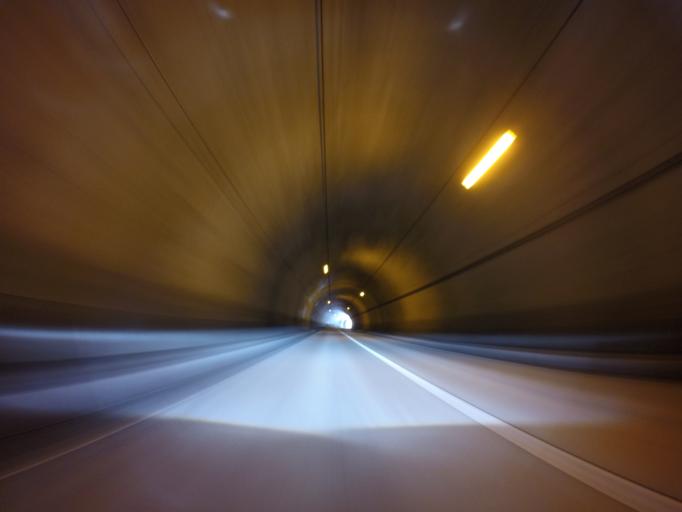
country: JP
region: Shizuoka
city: Shizuoka-shi
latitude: 35.2257
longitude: 138.3473
